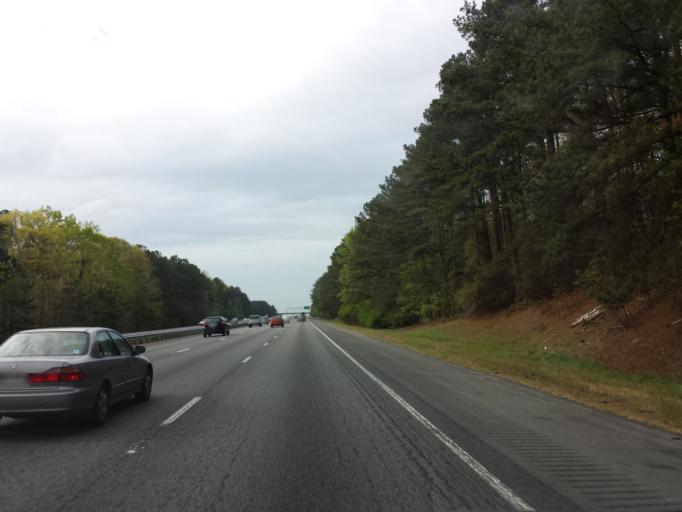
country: US
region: Georgia
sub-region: Butts County
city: Indian Springs
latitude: 33.1580
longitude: -84.0359
